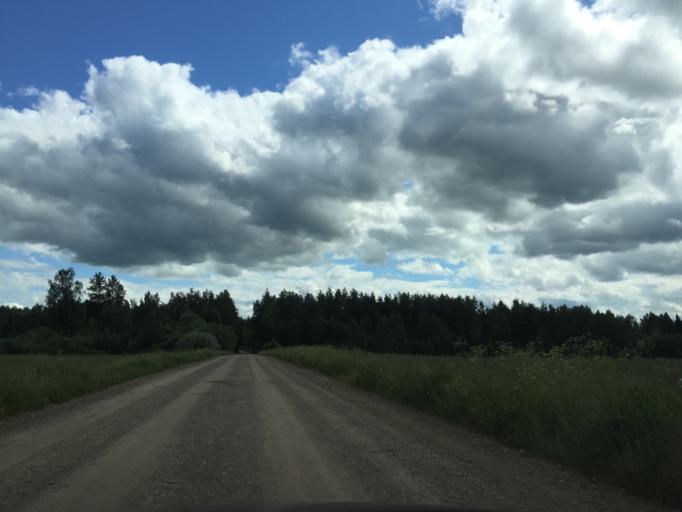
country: LV
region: Vecumnieki
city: Vecumnieki
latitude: 56.4976
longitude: 24.4075
